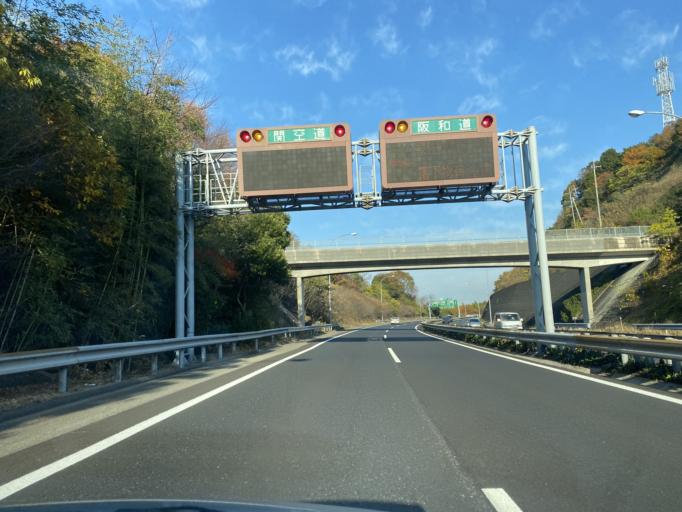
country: JP
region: Osaka
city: Kaizuka
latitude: 34.3630
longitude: 135.3260
